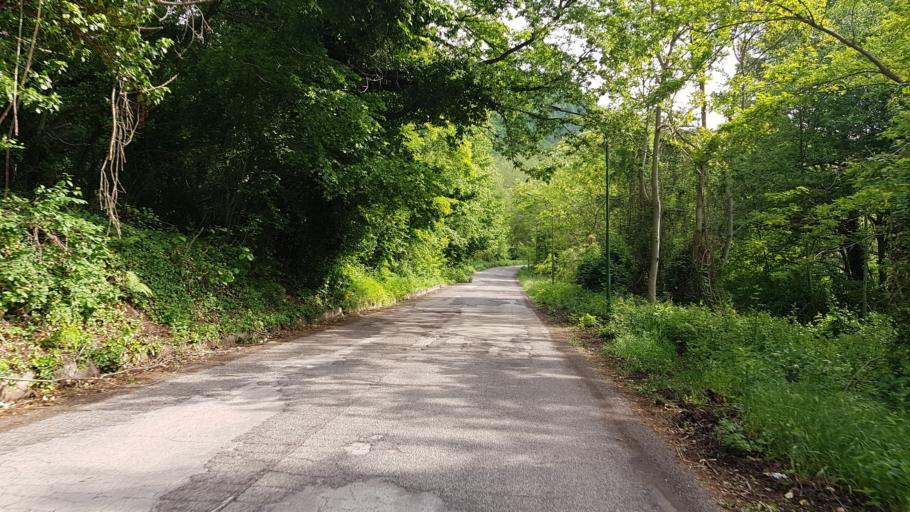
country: IT
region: Basilicate
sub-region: Provincia di Potenza
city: Zona 179
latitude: 40.9355
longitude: 15.6020
